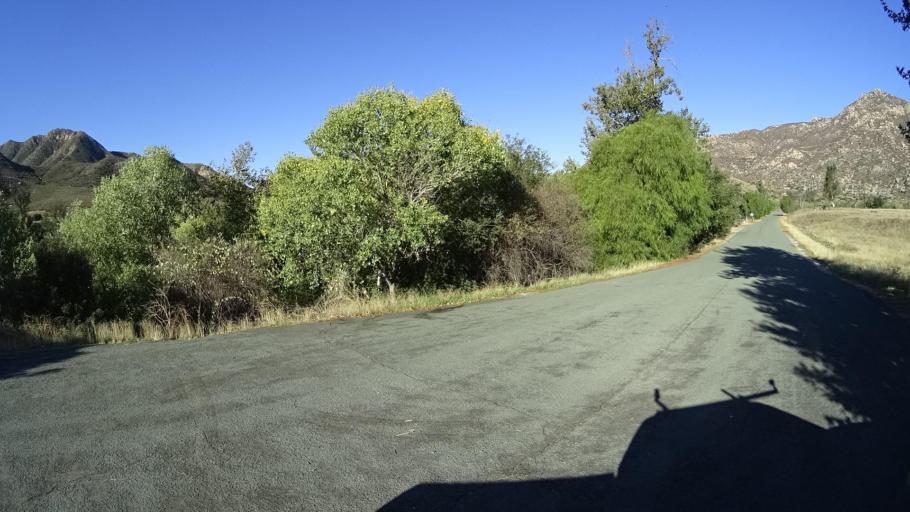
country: MX
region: Baja California
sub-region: Tecate
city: Lomas de Santa Anita
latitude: 32.6083
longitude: -116.6957
